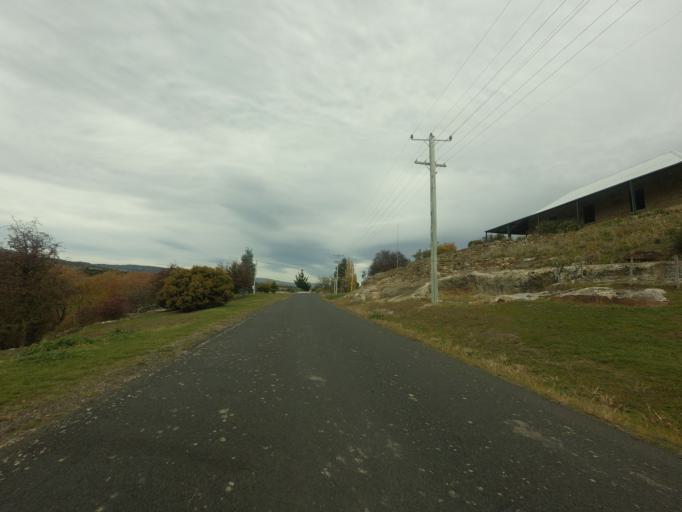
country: AU
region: Tasmania
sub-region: Derwent Valley
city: New Norfolk
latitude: -42.3812
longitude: 147.0002
